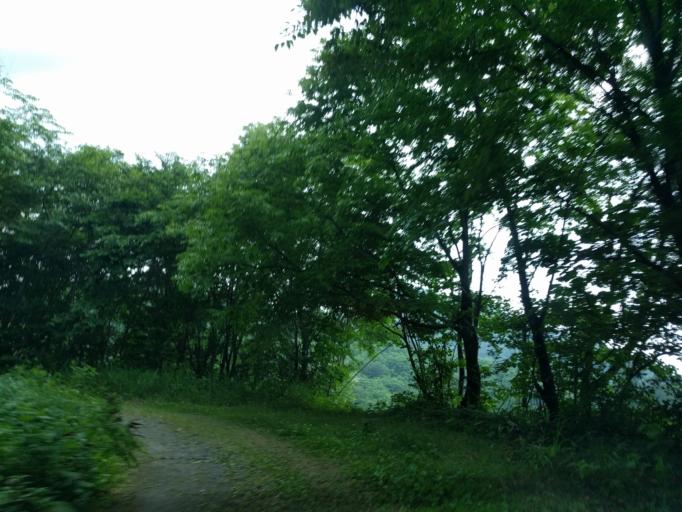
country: JP
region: Fukushima
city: Inawashiro
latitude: 37.4312
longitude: 140.0419
